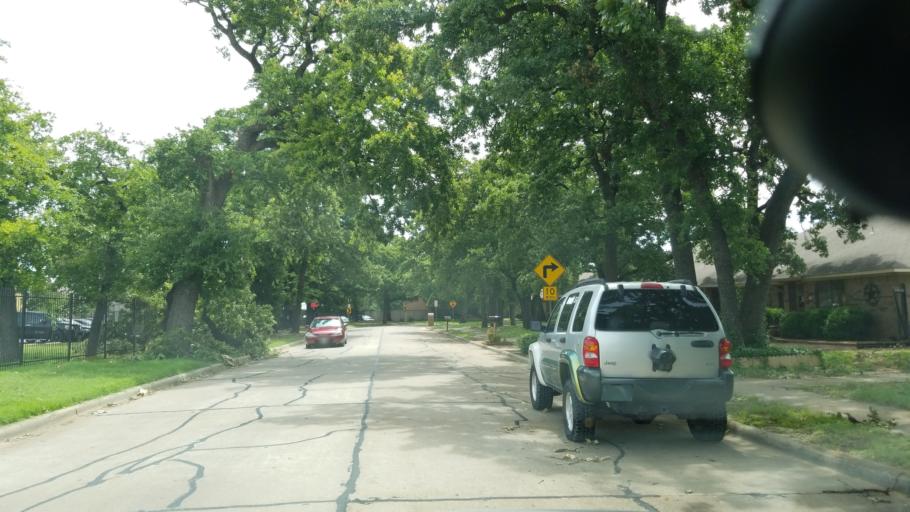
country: US
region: Texas
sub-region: Dallas County
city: Irving
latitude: 32.8336
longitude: -96.9288
